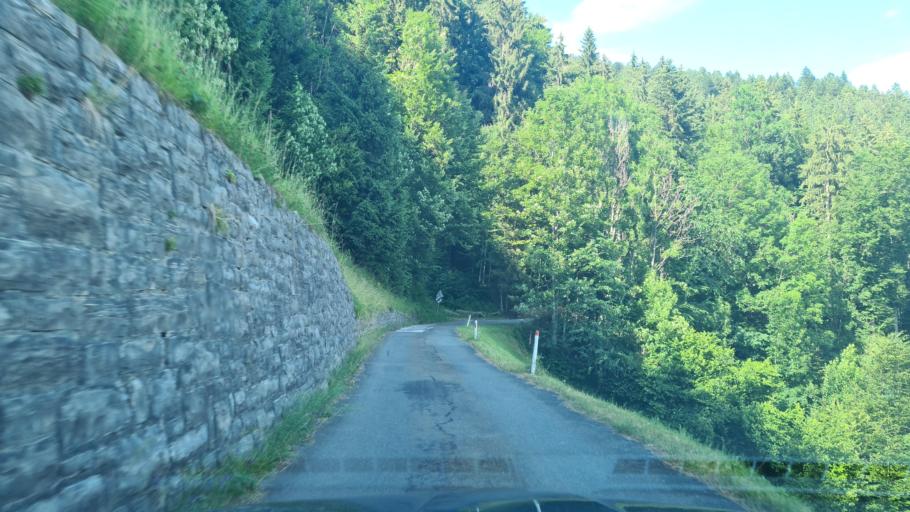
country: AT
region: Salzburg
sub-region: Politischer Bezirk Zell am See
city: Unken
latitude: 47.6509
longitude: 12.6994
